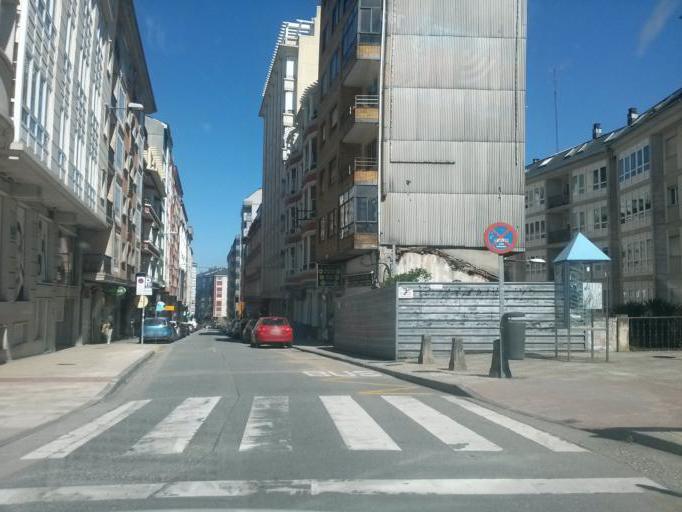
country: ES
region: Galicia
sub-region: Provincia de Lugo
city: Lugo
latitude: 43.0106
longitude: -7.5527
